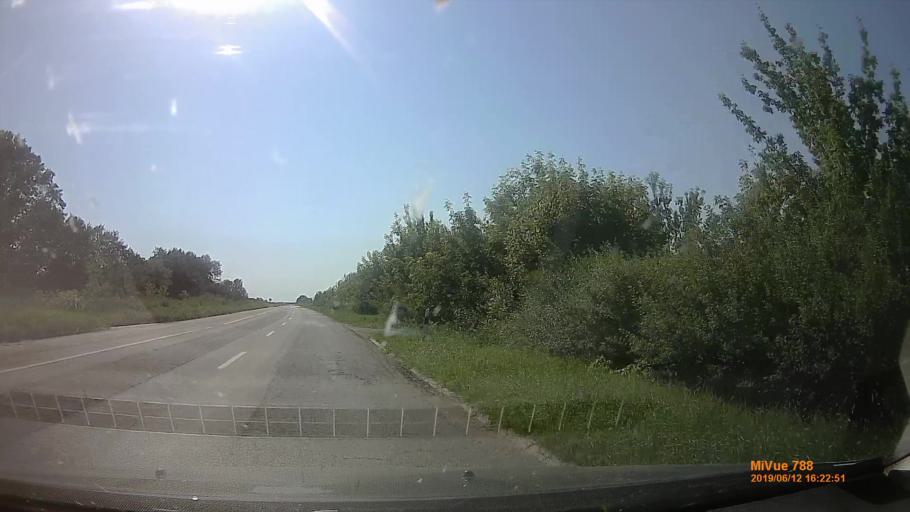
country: RO
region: Arad
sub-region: Comuna Nadlac
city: Nadlac
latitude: 46.1677
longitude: 20.6950
